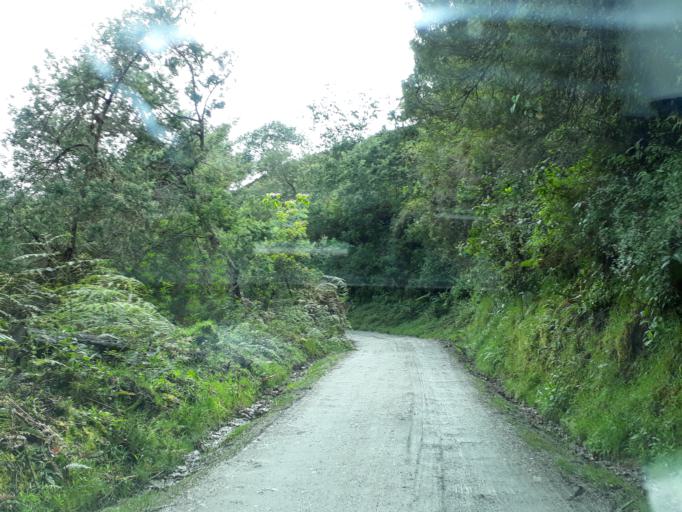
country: CO
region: Cundinamarca
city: Junin
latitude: 4.6864
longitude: -73.6771
